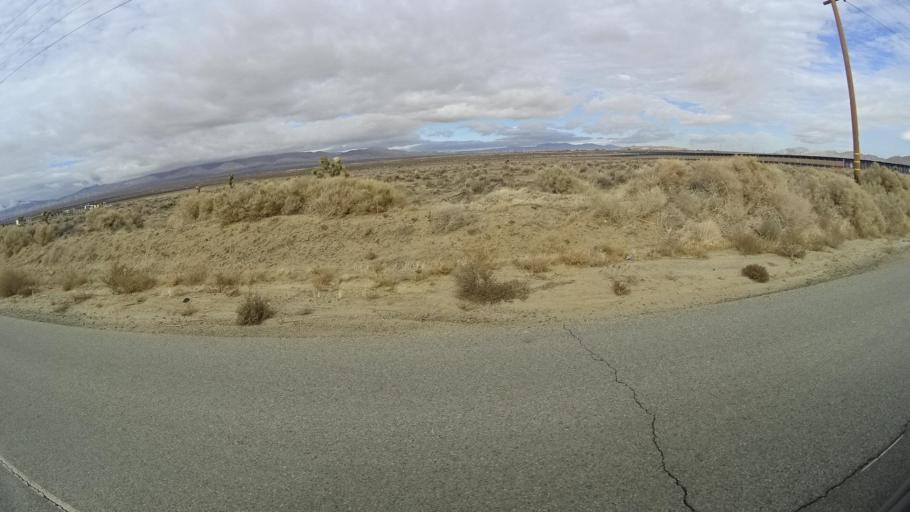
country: US
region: California
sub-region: Kern County
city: Rosamond
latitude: 34.8633
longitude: -118.3337
